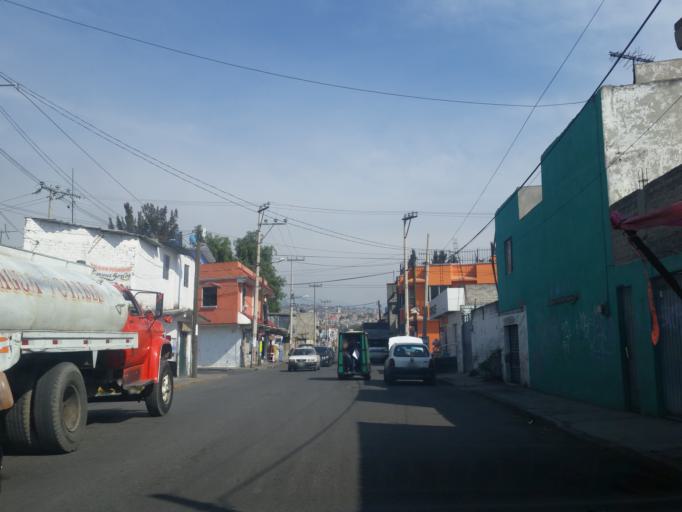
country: MX
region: Mexico
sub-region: La Paz
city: San Isidro
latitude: 19.3242
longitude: -98.9531
